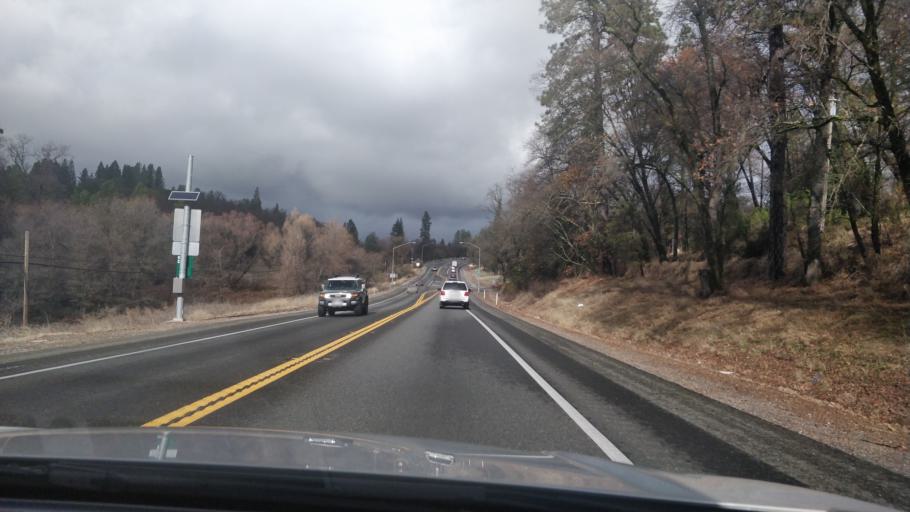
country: US
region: California
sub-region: Nevada County
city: Alta Sierra
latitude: 39.1229
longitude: -121.0784
